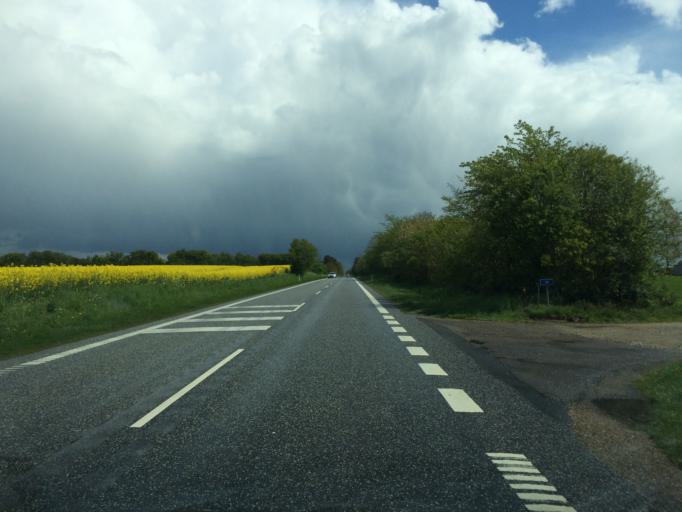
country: DK
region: Central Jutland
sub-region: Skive Kommune
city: Hojslev
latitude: 56.5783
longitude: 9.1443
